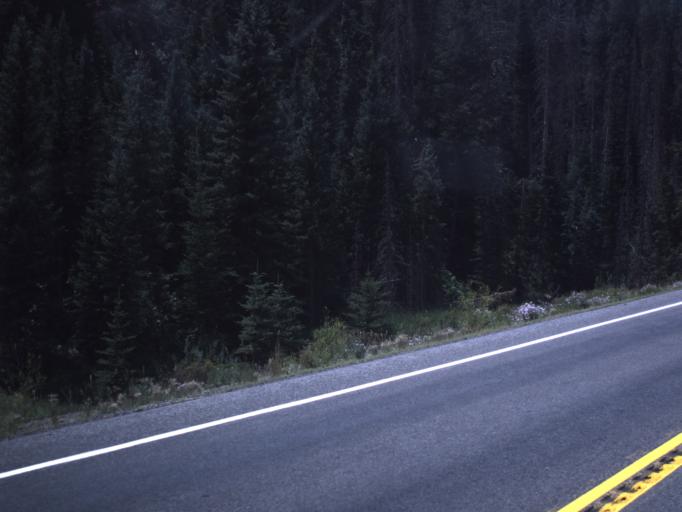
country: US
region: Utah
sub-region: Sanpete County
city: Fairview
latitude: 39.6836
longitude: -111.1673
